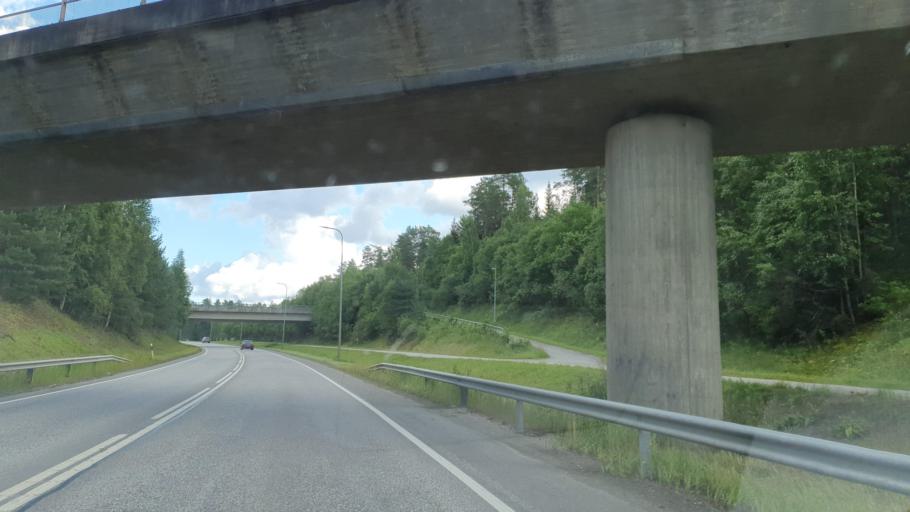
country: FI
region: Kainuu
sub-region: Kajaani
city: Kajaani
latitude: 64.2175
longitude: 27.6989
